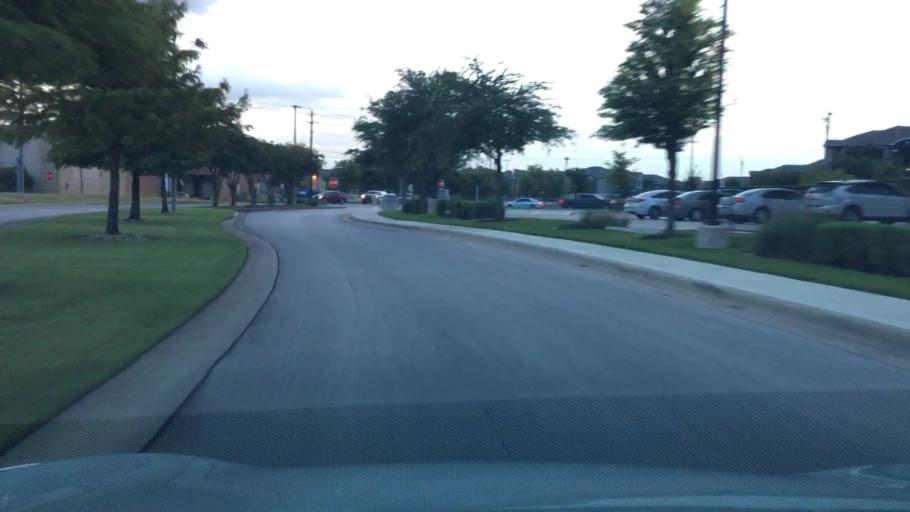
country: US
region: Texas
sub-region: Travis County
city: Onion Creek
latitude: 30.1634
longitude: -97.7954
